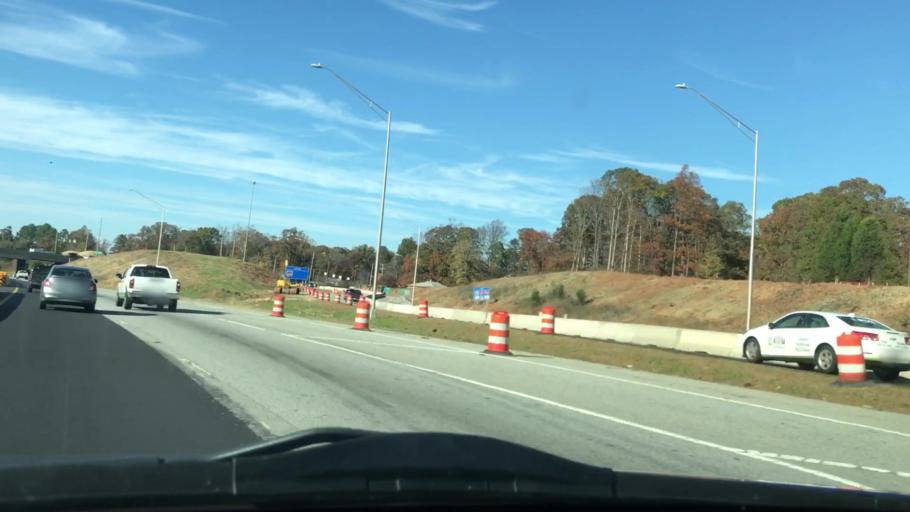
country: US
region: North Carolina
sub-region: Guilford County
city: High Point
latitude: 36.0002
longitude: -79.9901
